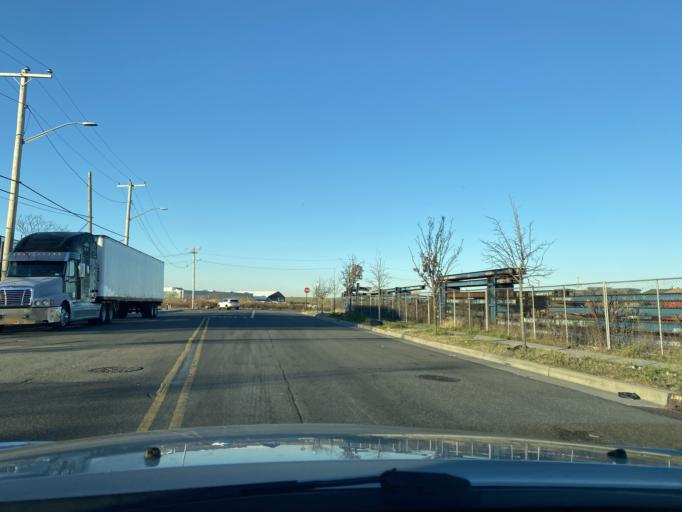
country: US
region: New York
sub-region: Nassau County
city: Inwood
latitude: 40.5958
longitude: -73.7800
